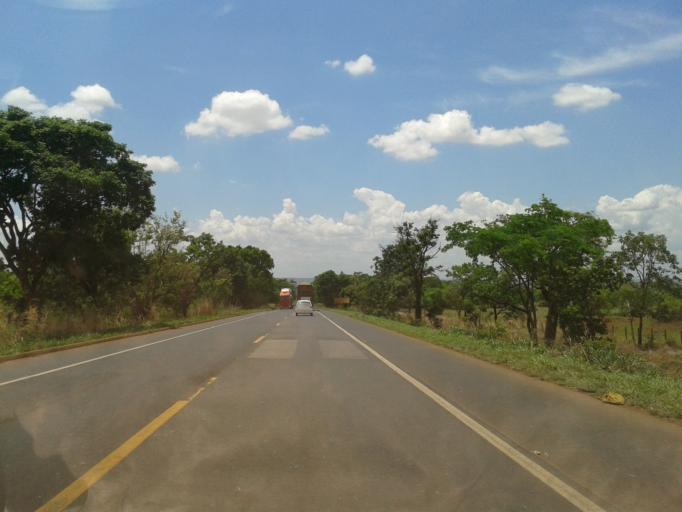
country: BR
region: Goias
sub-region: Goiatuba
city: Goiatuba
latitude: -18.2634
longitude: -49.6601
